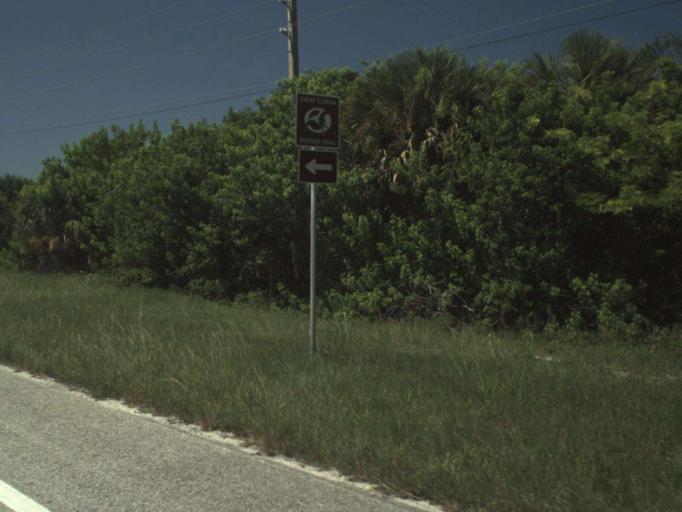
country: US
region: Florida
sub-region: Saint Lucie County
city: Lakewood Park
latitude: 27.5284
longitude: -80.3595
